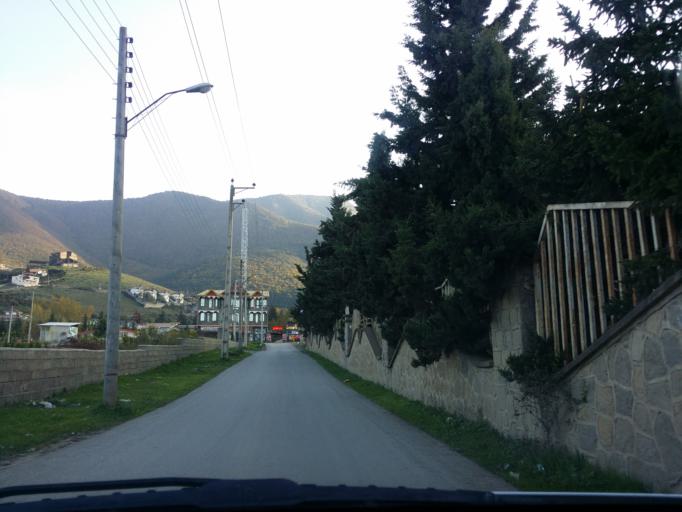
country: IR
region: Mazandaran
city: `Abbasabad
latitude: 36.5089
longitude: 51.1758
